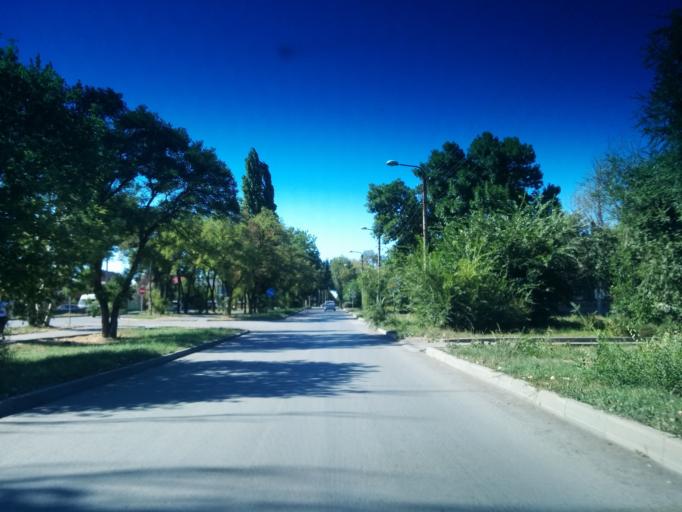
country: RU
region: Rostov
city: Shakhty
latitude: 47.7047
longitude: 40.2287
